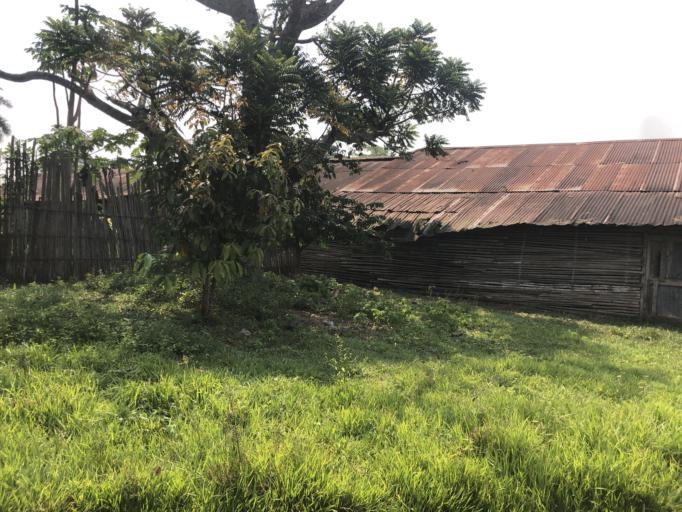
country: CD
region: Bandundu
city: Kikwit
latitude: -5.5388
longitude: 19.2227
